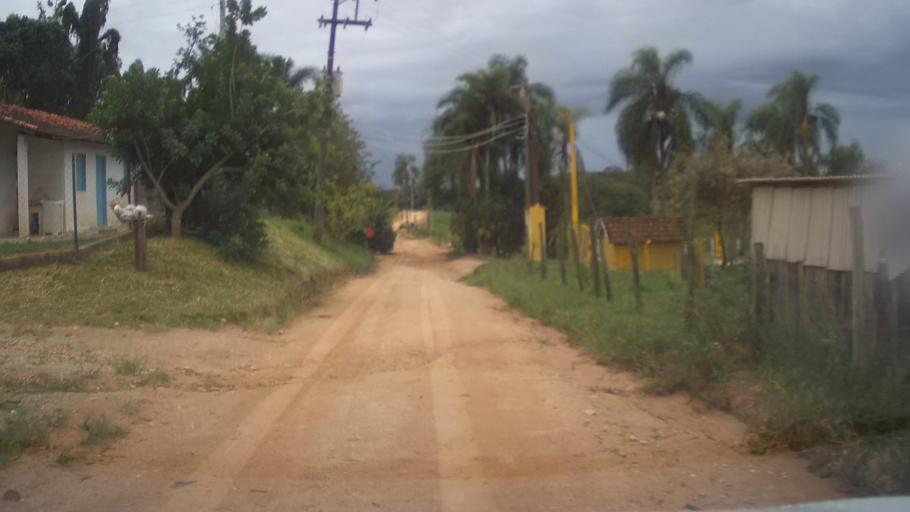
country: BR
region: Sao Paulo
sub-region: Itupeva
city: Itupeva
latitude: -23.1861
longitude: -47.0589
